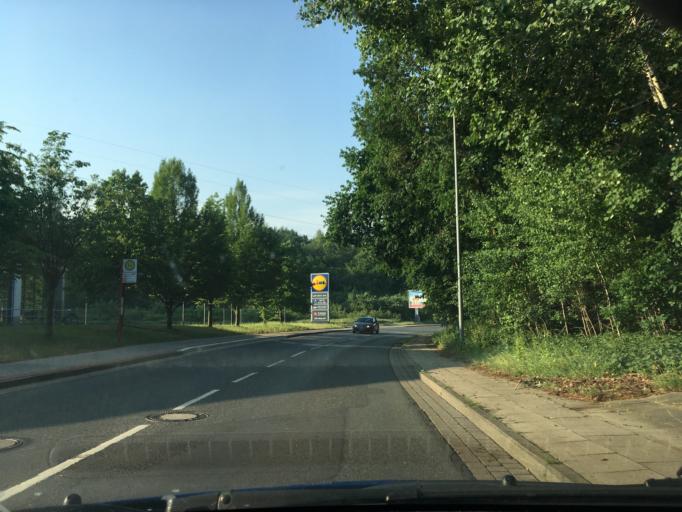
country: DE
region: Lower Saxony
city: Buchholz in der Nordheide
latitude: 53.3453
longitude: 9.8573
